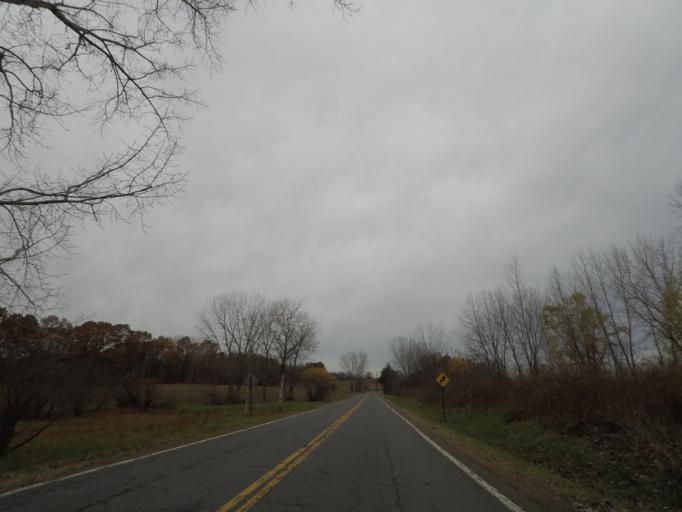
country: US
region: New York
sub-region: Saratoga County
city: Mechanicville
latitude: 42.8509
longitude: -73.6971
